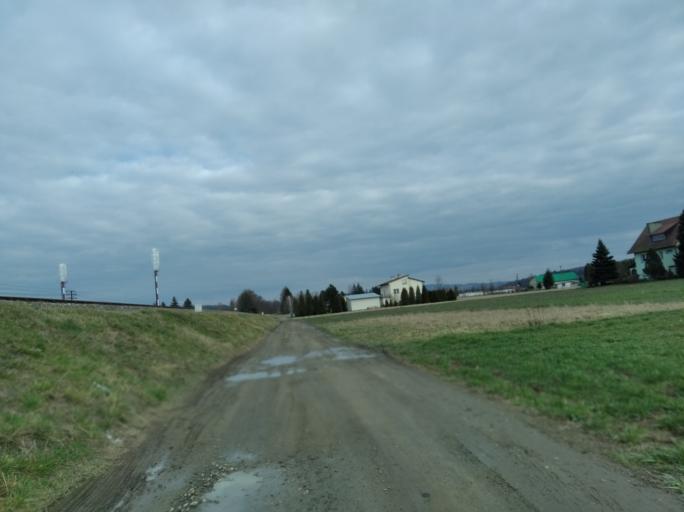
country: PL
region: Subcarpathian Voivodeship
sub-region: Powiat strzyzowski
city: Wysoka Strzyzowska
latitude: 49.8732
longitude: 21.7353
